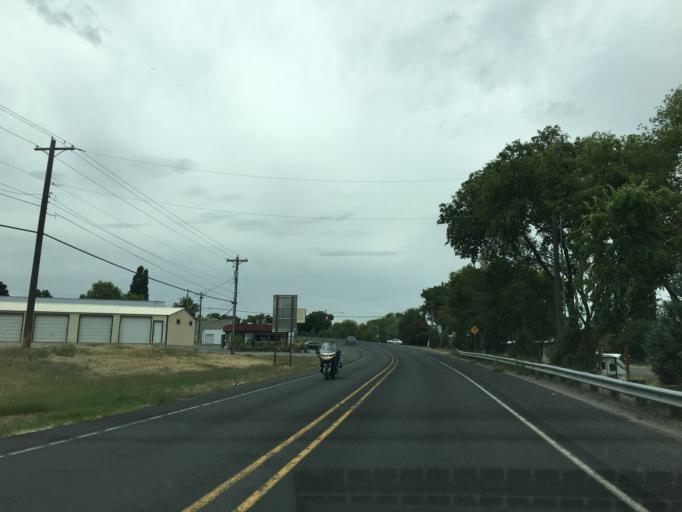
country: US
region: Washington
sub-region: Okanogan County
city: Coulee Dam
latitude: 47.9342
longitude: -119.0318
